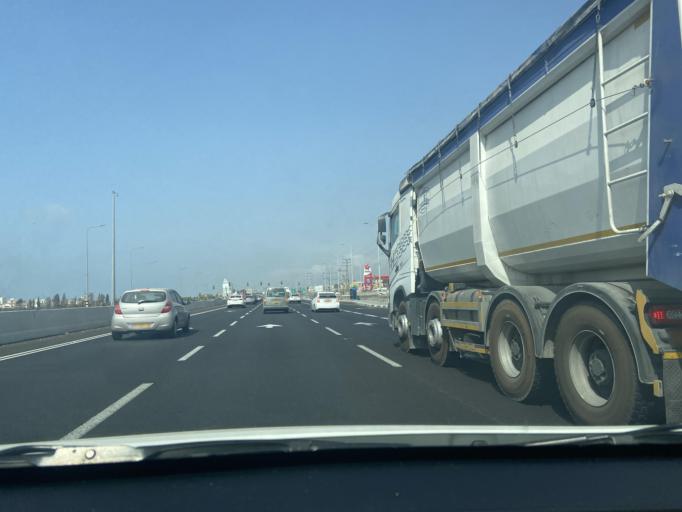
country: IL
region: Northern District
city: El Mazra`a
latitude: 32.9764
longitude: 35.0935
